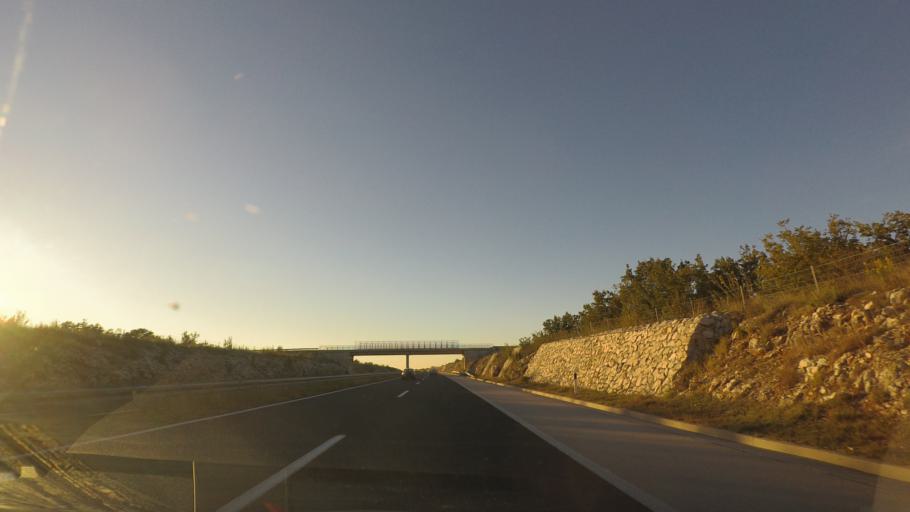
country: HR
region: Zadarska
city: Polaca
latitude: 44.0874
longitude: 15.4983
